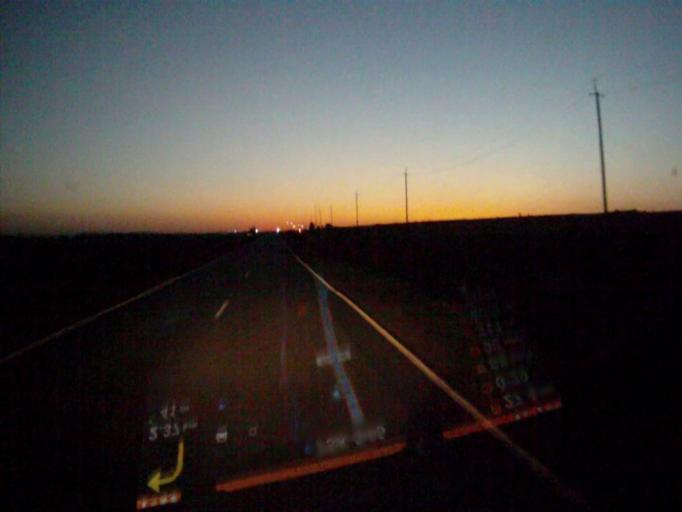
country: RU
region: Chelyabinsk
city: Chebarkul'
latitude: 55.2220
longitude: 60.4859
